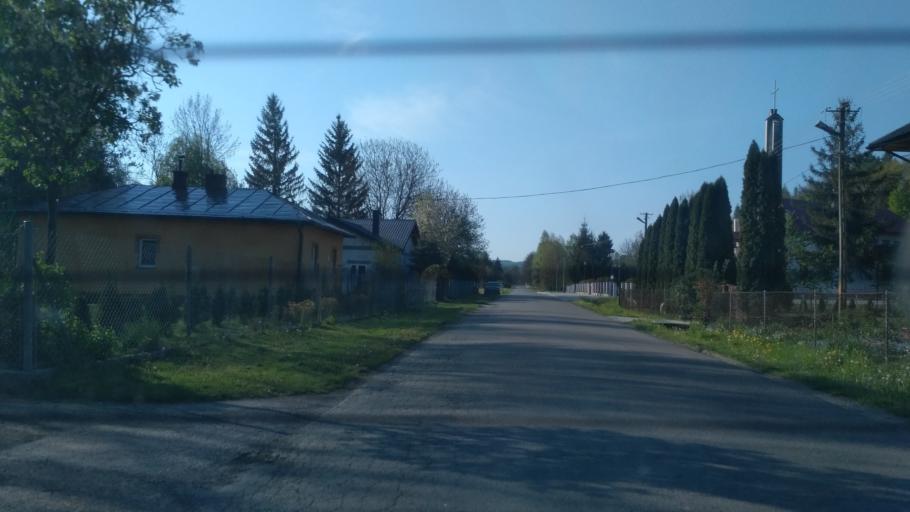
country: PL
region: Subcarpathian Voivodeship
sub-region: Powiat jaroslawski
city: Pruchnik
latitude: 49.8903
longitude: 22.5587
